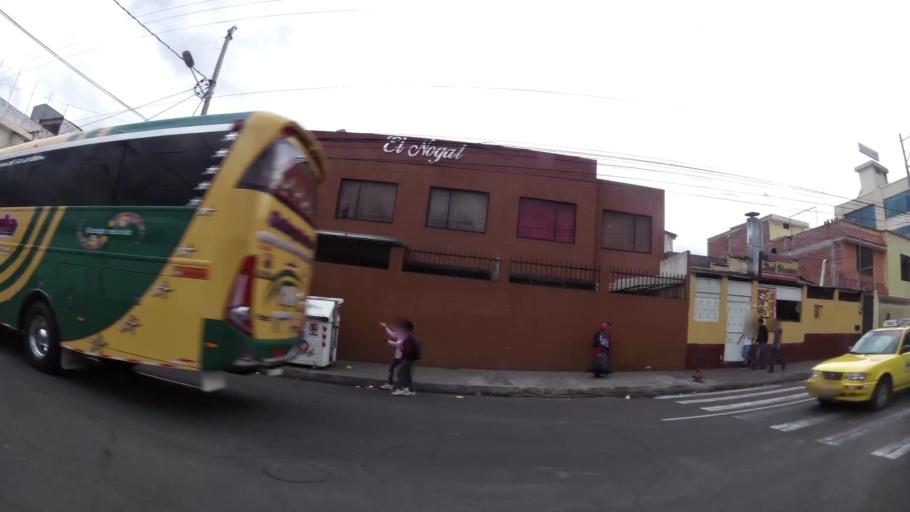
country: EC
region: Tungurahua
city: Ambato
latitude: -1.2314
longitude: -78.6209
